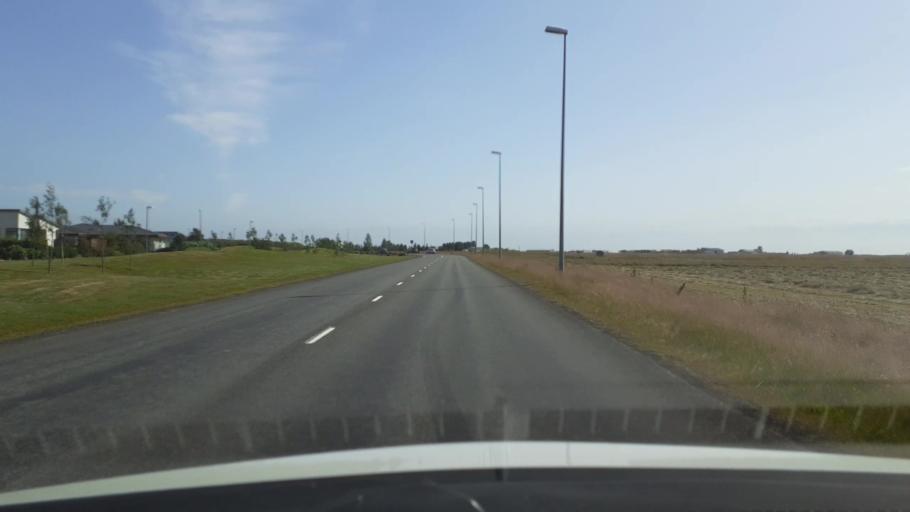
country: IS
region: South
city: Selfoss
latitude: 63.9235
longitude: -21.0093
